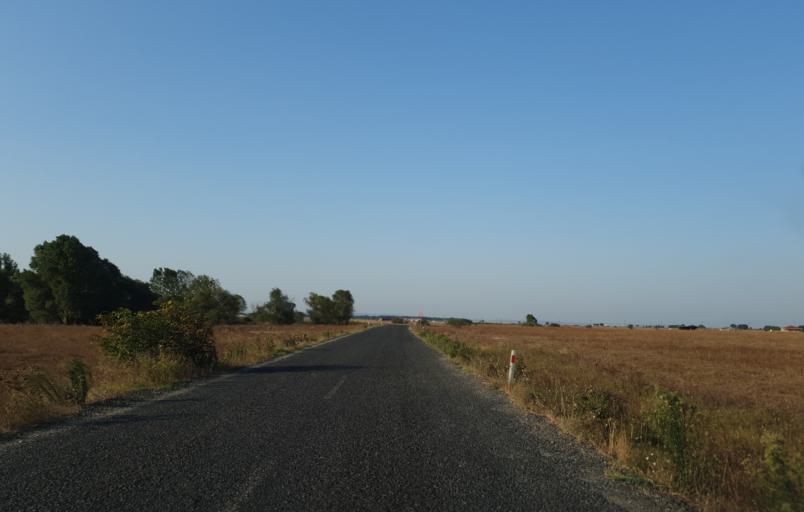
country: TR
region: Tekirdag
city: Beyazkoy
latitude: 41.4146
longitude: 27.7633
